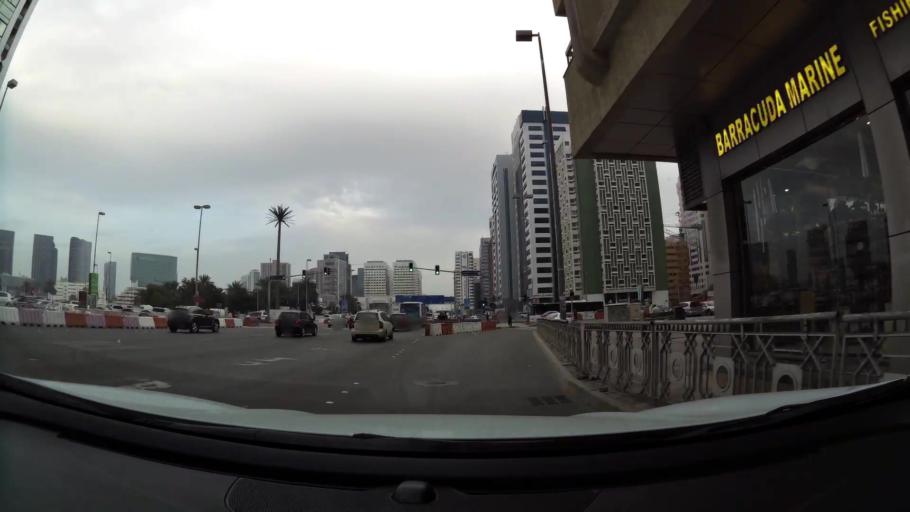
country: AE
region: Abu Dhabi
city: Abu Dhabi
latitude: 24.5002
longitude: 54.3768
